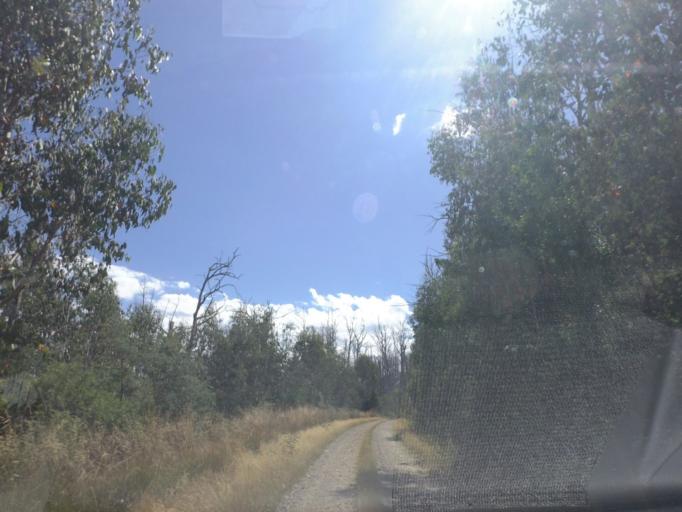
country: AU
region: Victoria
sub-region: Murrindindi
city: Alexandra
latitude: -37.4613
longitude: 145.8179
